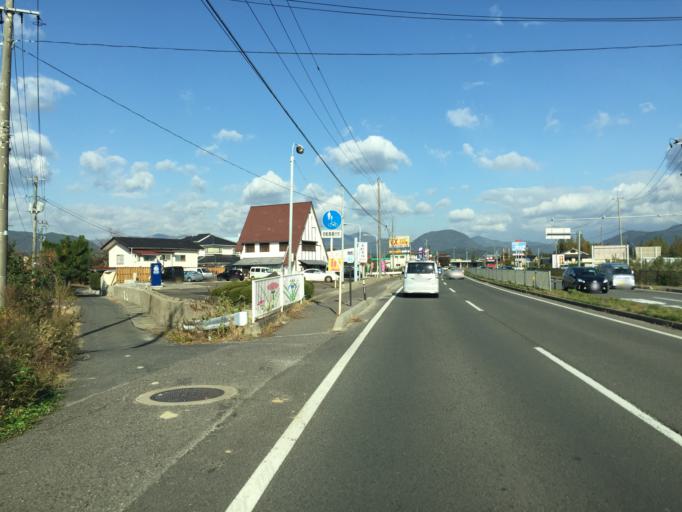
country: JP
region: Fukushima
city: Fukushima-shi
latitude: 37.7982
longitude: 140.4561
